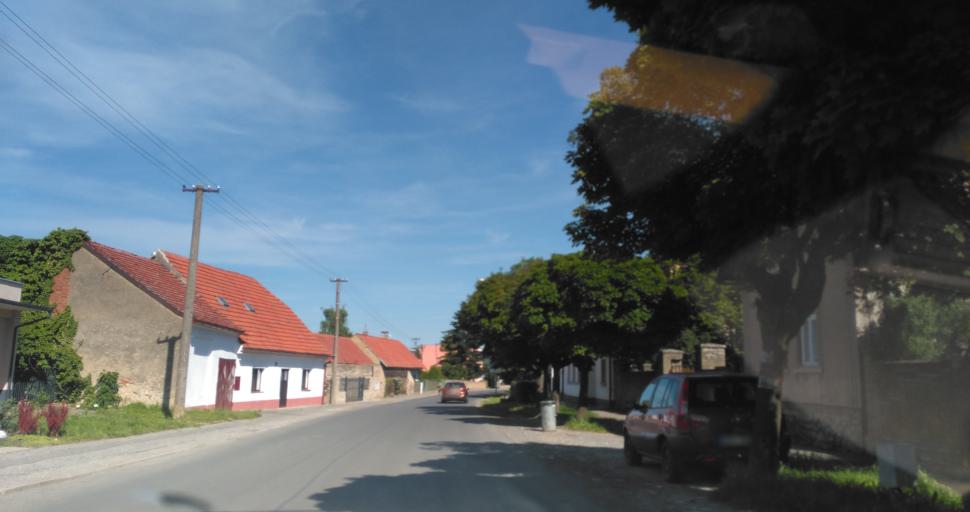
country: CZ
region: Central Bohemia
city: Revnice
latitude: 49.9036
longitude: 14.1505
